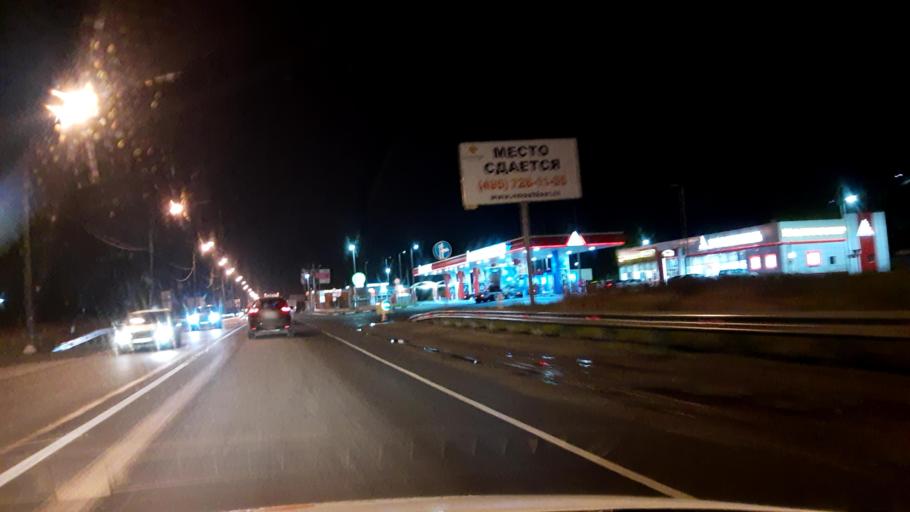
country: RU
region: Moskovskaya
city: Elektrostal'
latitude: 55.8149
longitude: 38.4259
